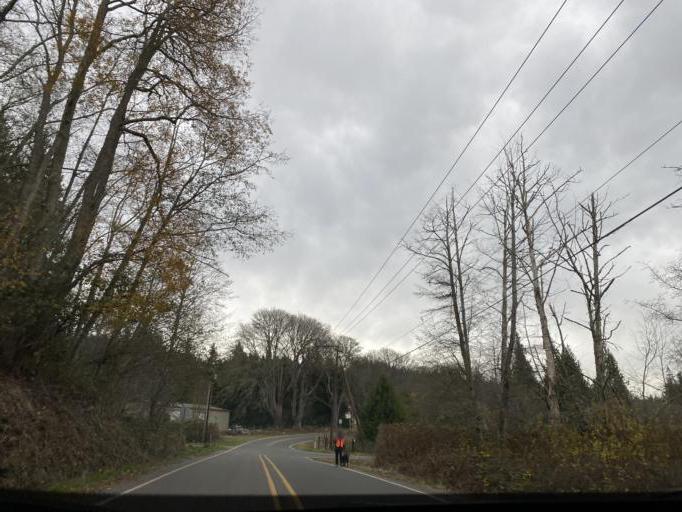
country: US
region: Washington
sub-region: Island County
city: Freeland
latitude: 48.0142
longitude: -122.5079
